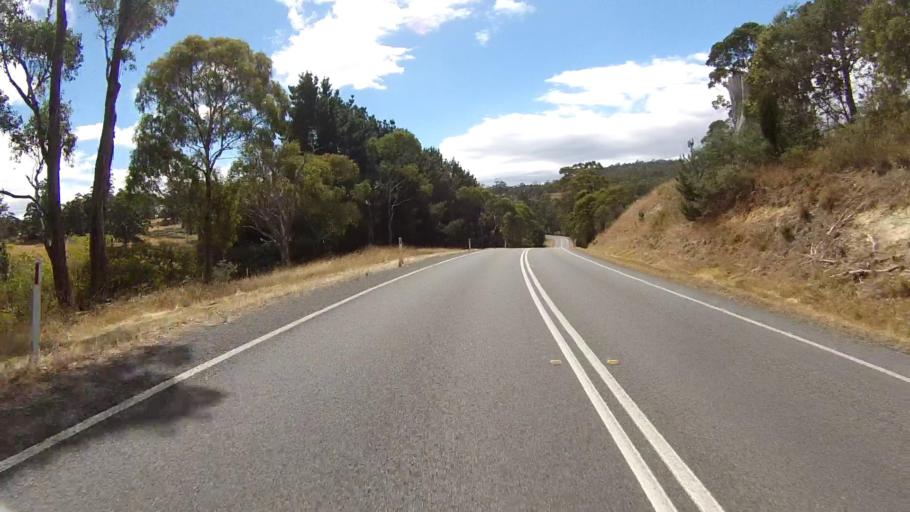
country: AU
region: Tasmania
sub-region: Sorell
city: Sorell
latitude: -42.6287
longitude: 147.6290
